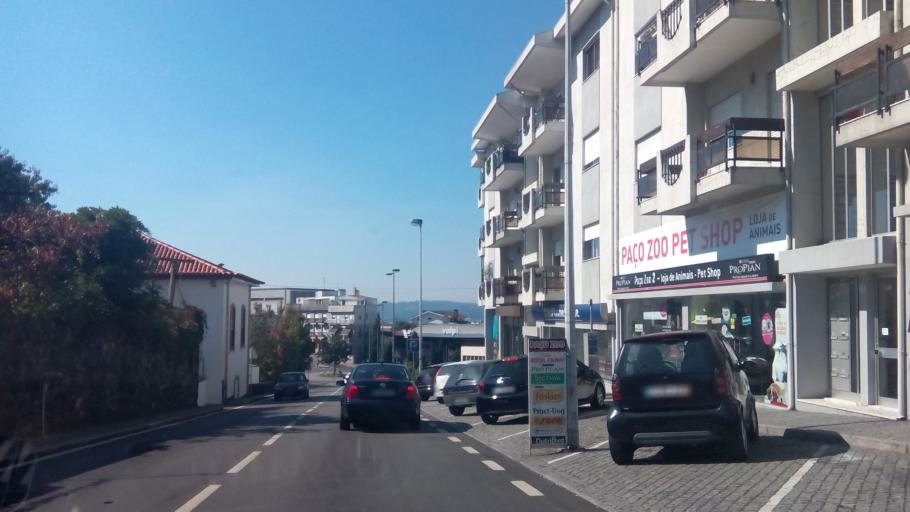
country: PT
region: Porto
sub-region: Penafiel
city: Penafiel
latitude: 41.2073
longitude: -8.2807
